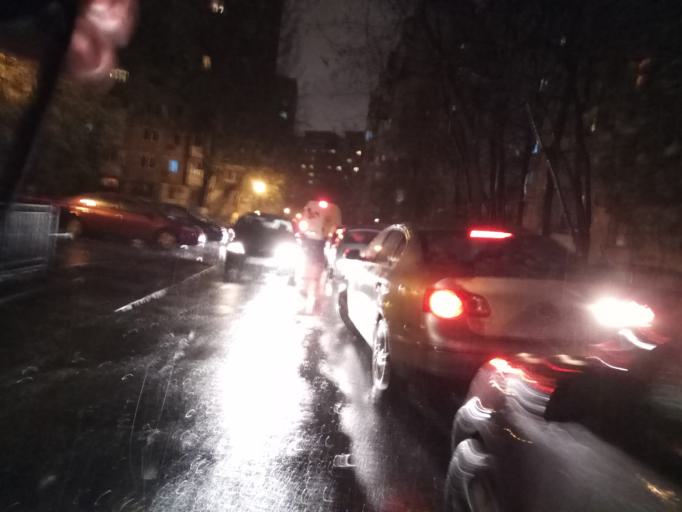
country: RO
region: Ilfov
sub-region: Comuna Chiajna
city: Rosu
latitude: 44.4329
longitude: 26.0256
